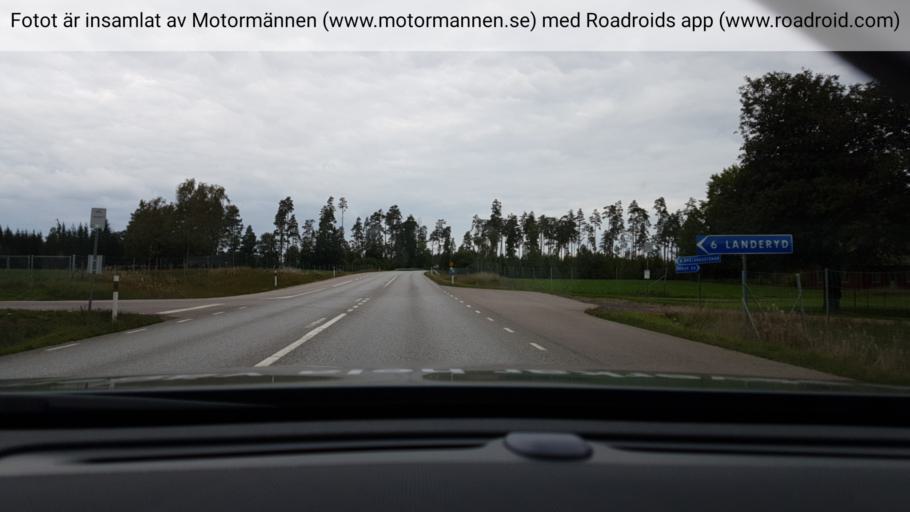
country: SE
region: Joenkoeping
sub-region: Gislaveds Kommun
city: Smalandsstenar
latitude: 57.0908
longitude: 13.3708
